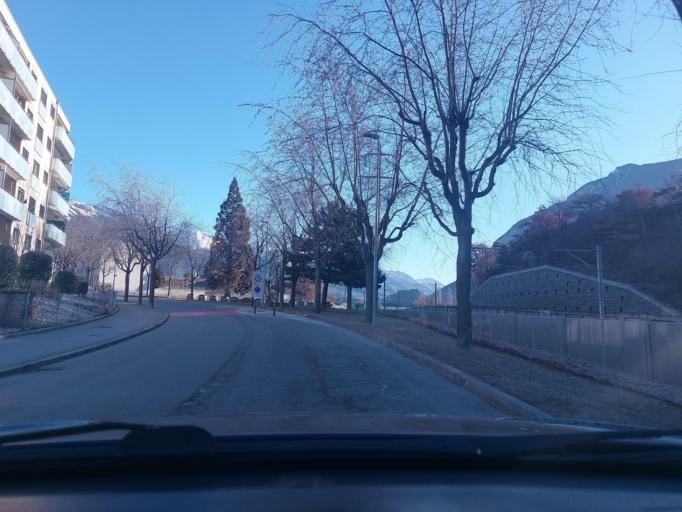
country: CH
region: Valais
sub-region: Sierre District
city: Chalais
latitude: 46.2823
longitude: 7.5170
